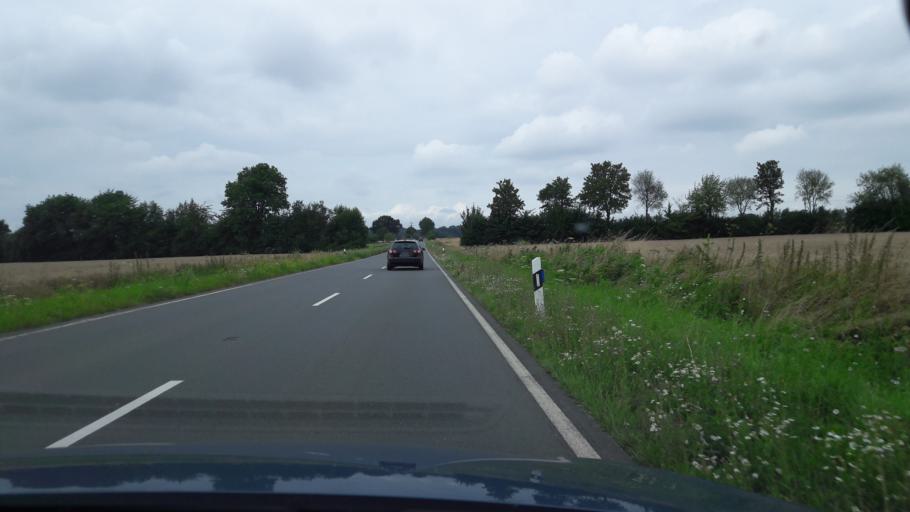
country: DE
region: North Rhine-Westphalia
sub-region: Regierungsbezirk Munster
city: Ennigerloh
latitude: 51.8438
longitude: 8.0035
